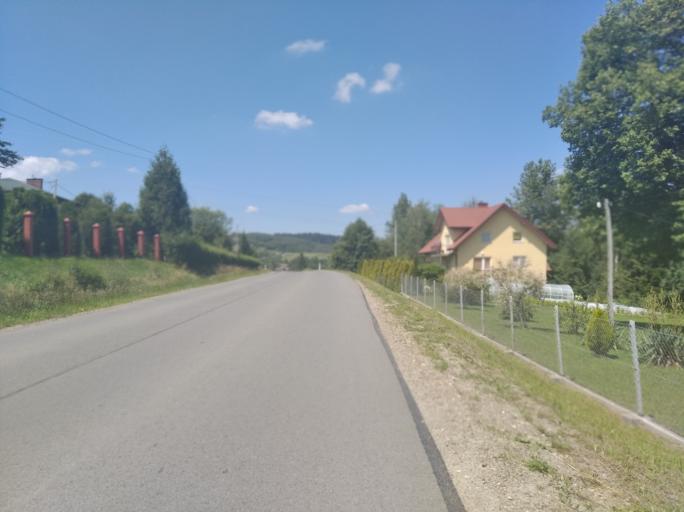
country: PL
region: Subcarpathian Voivodeship
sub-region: Powiat brzozowski
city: Jablonka
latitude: 49.6982
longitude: 22.1335
